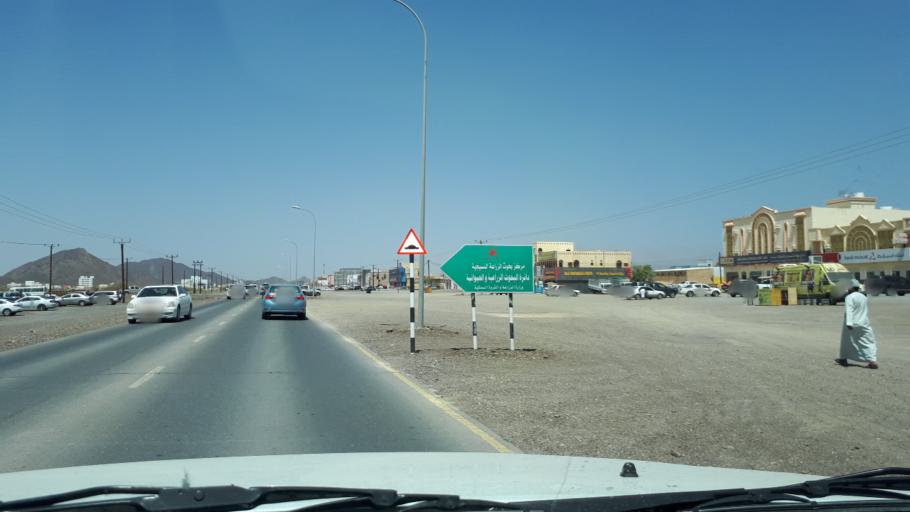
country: OM
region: Muhafazat ad Dakhiliyah
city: Bahla'
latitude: 22.9474
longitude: 57.2737
